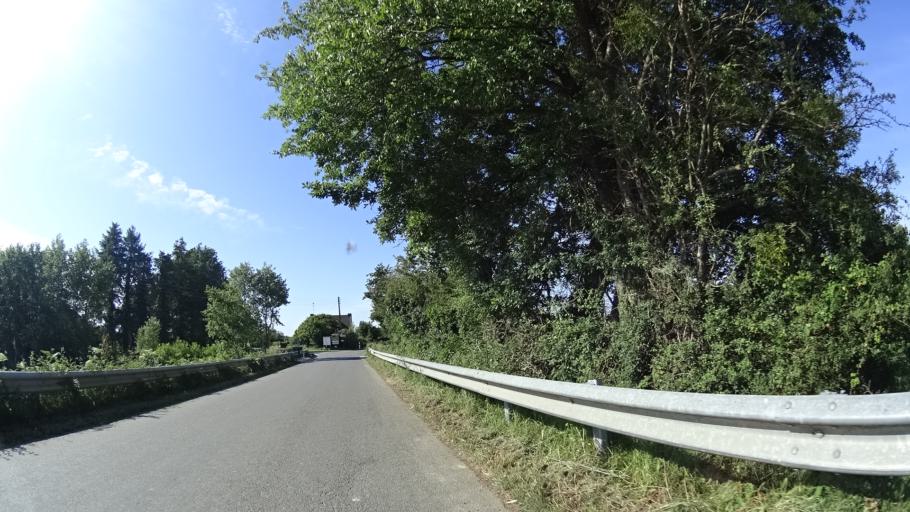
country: FR
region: Brittany
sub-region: Departement d'Ille-et-Vilaine
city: Guipry
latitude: 47.8123
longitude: -1.8507
